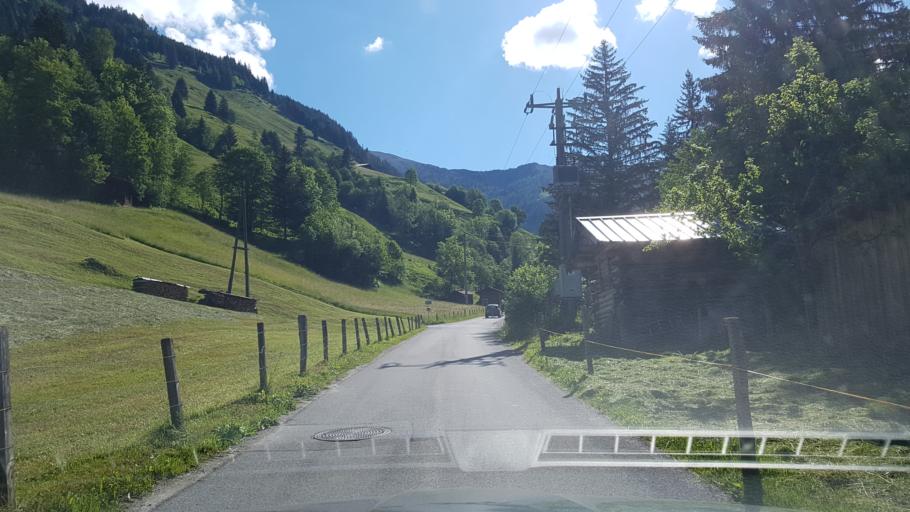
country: AT
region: Salzburg
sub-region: Politischer Bezirk Sankt Johann im Pongau
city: Huttschlag
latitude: 47.2351
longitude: 13.2465
